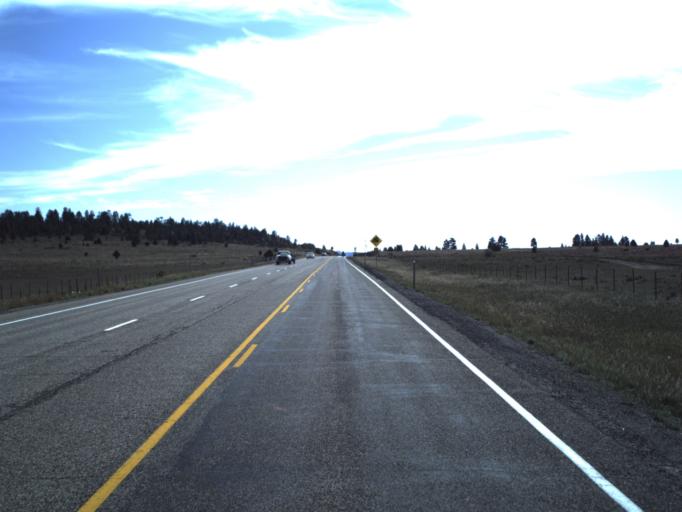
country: US
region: Utah
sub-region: Garfield County
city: Panguitch
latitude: 37.6883
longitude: -112.1420
